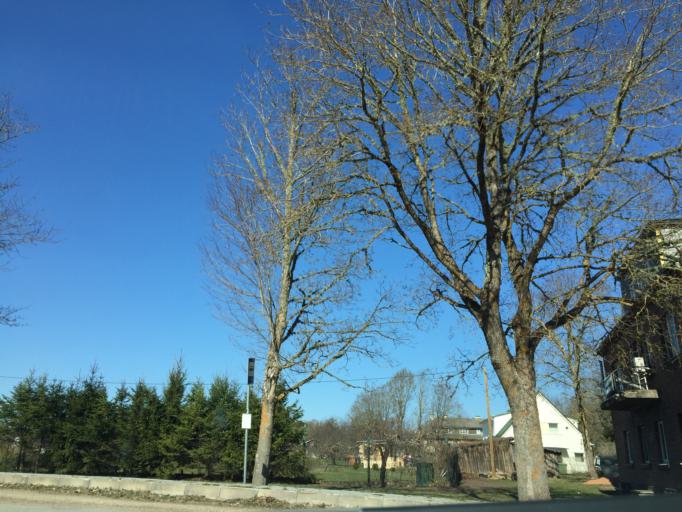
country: EE
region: Tartu
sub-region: Puhja vald
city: Puhja
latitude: 58.3629
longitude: 26.4330
